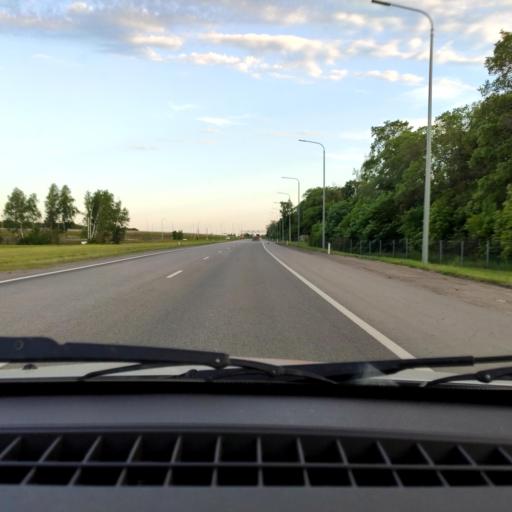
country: RU
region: Voronezj
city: Podgornoye
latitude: 51.8409
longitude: 39.2140
